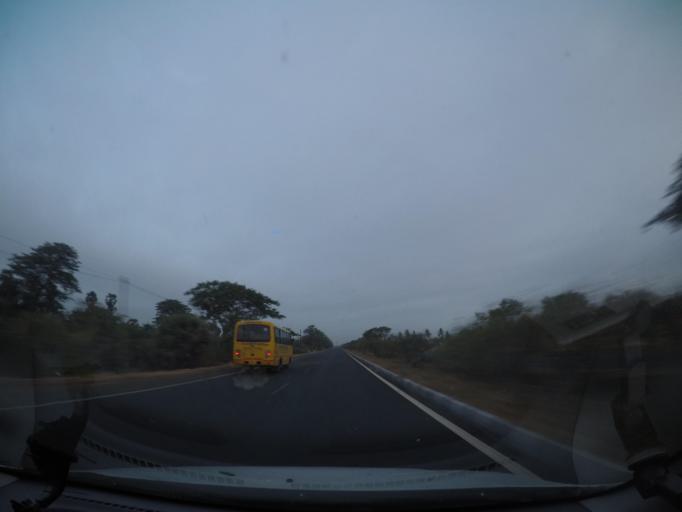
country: IN
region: Andhra Pradesh
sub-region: West Godavari
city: Tadepallegudem
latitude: 16.8101
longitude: 81.3443
